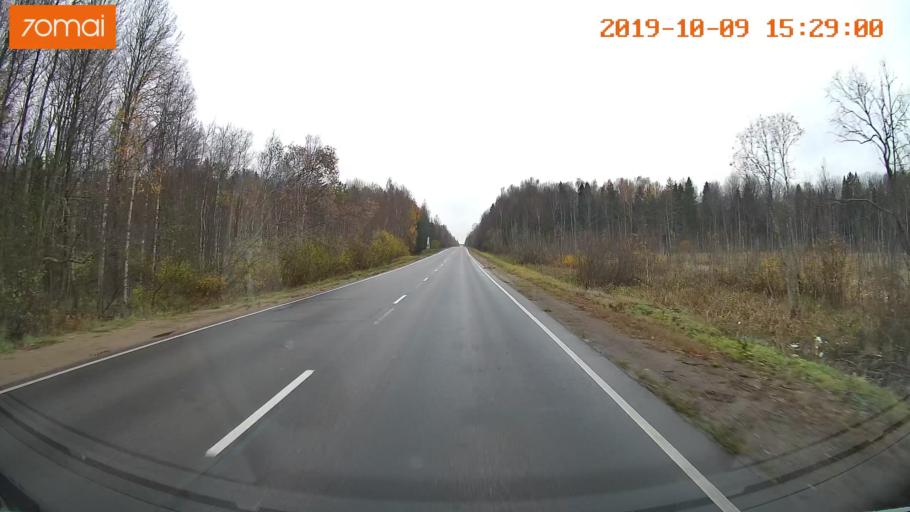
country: RU
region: Kostroma
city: Susanino
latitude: 57.9966
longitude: 41.3504
